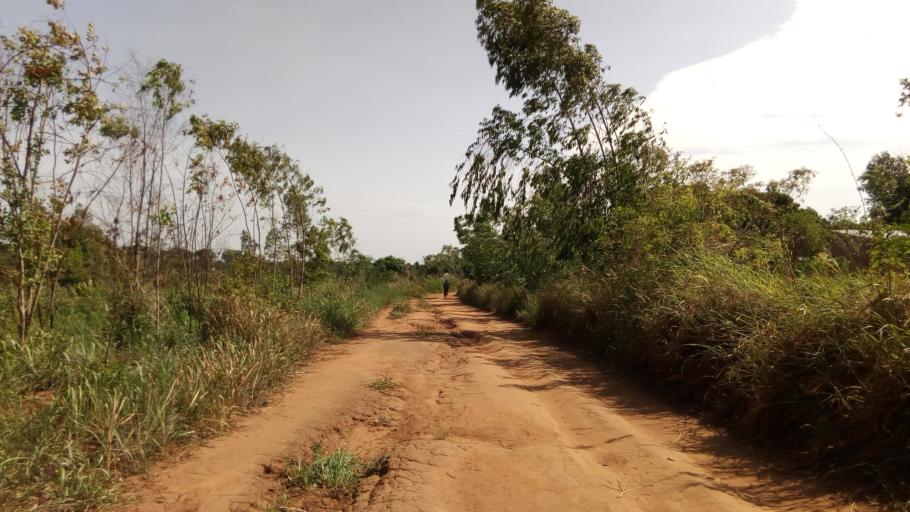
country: UG
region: Northern Region
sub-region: Gulu District
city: Gulu
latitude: 2.8009
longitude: 32.3284
